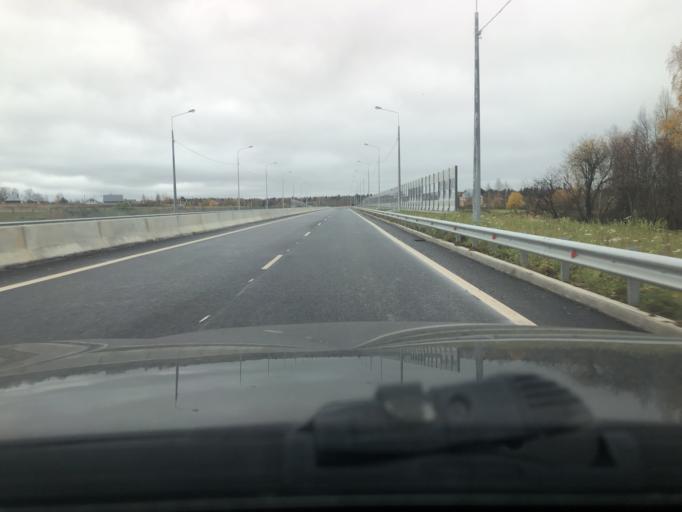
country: RU
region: Moskovskaya
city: Semkhoz
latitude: 56.3283
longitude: 38.0775
